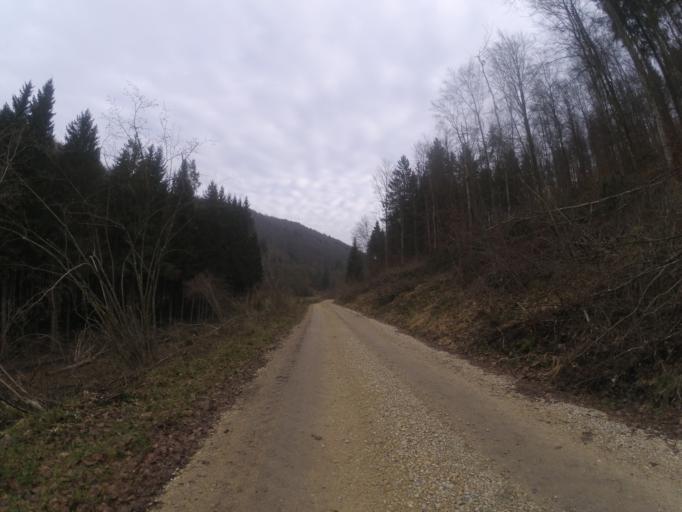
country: DE
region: Baden-Wuerttemberg
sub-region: Tuebingen Region
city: Mehrstetten
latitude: 48.3579
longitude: 9.5756
